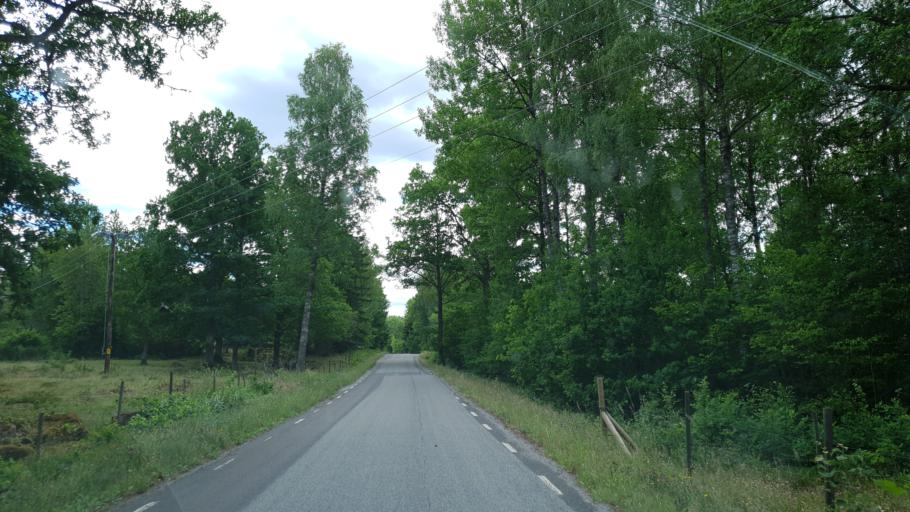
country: SE
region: Kalmar
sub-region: Hultsfreds Kommun
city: Virserum
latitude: 57.0562
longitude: 15.5882
